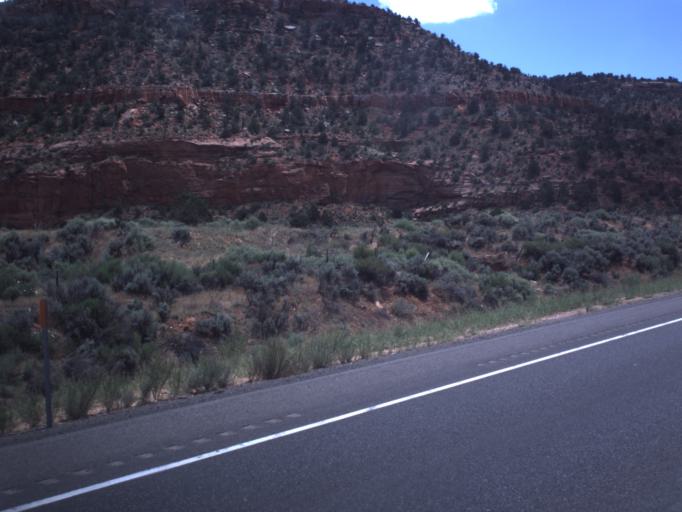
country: US
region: Utah
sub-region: Kane County
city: Kanab
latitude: 37.0698
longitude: -112.5368
